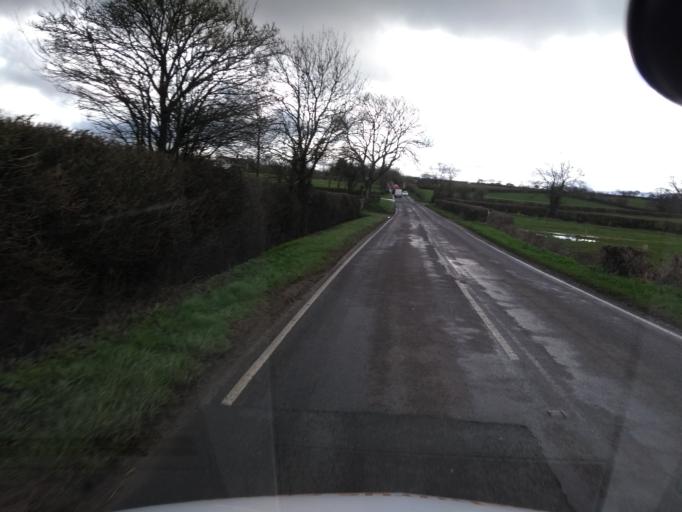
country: GB
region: England
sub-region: Dorset
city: Sherborne
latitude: 50.9305
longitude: -2.4972
